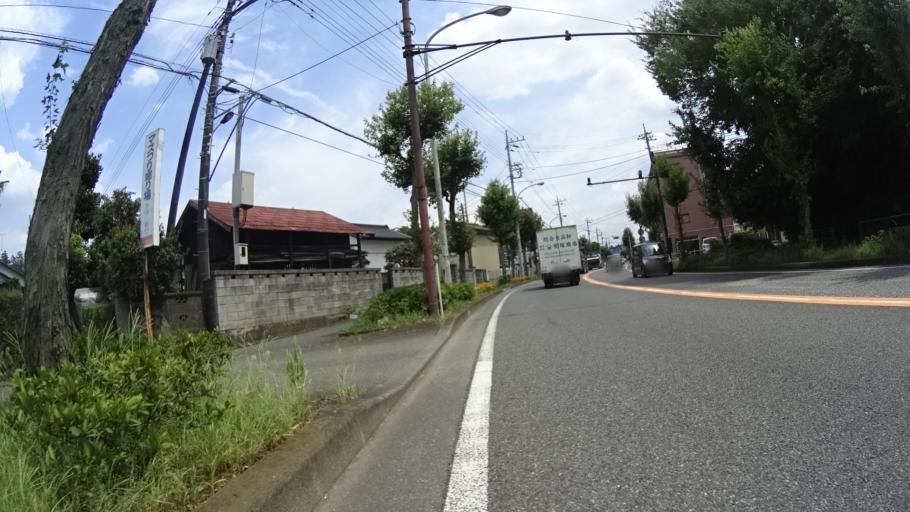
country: JP
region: Tokyo
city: Fussa
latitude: 35.7723
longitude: 139.2943
